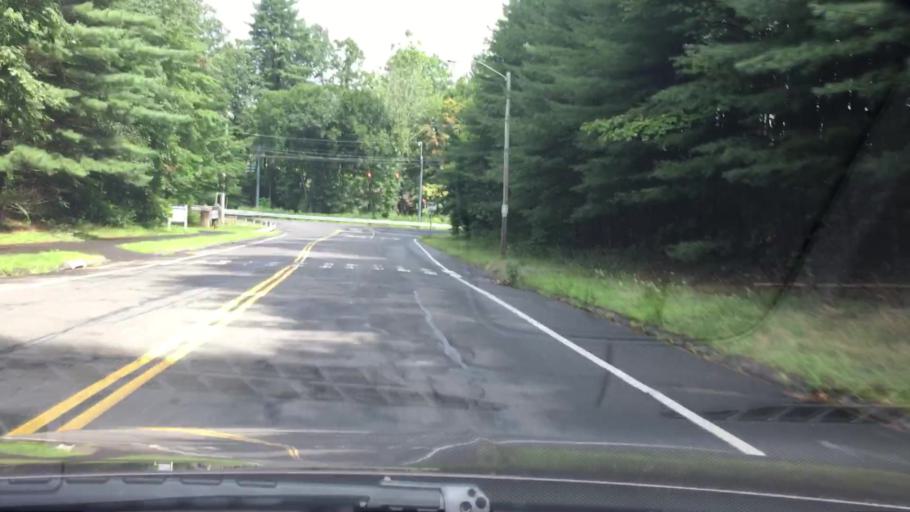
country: US
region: Connecticut
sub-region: Hartford County
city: Weatogue
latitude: 41.8096
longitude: -72.8376
